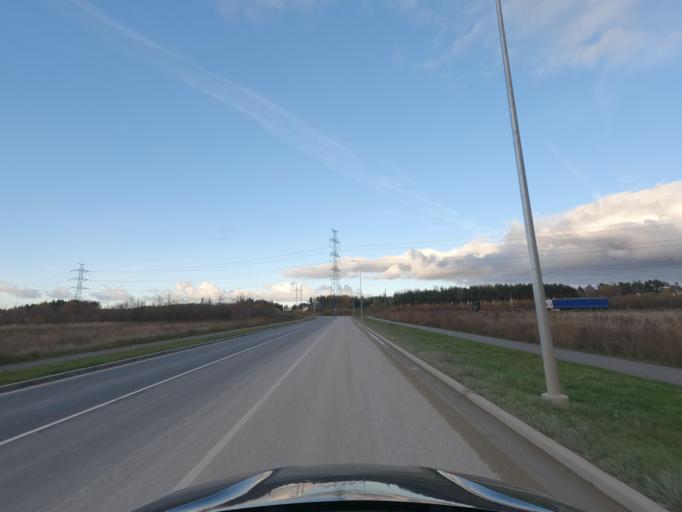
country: EE
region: Harju
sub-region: Saue vald
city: Laagri
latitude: 59.3368
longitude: 24.6028
